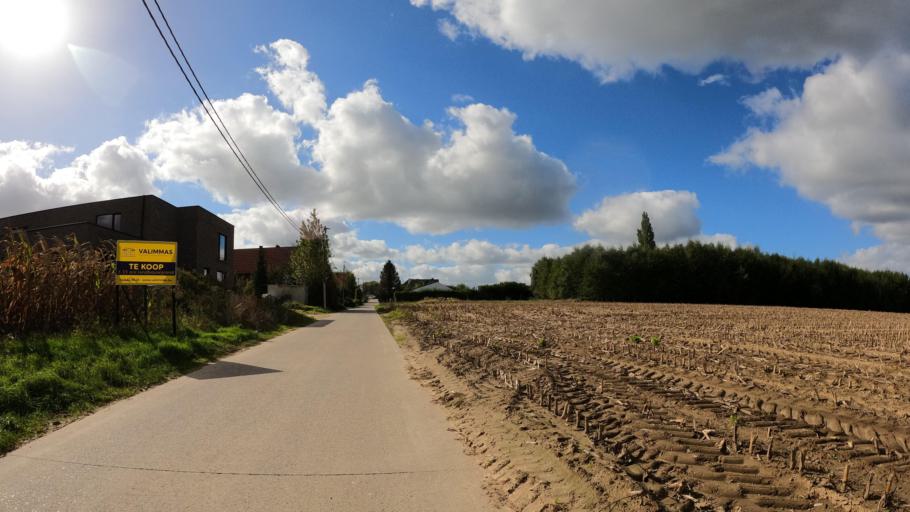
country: BE
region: Flanders
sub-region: Provincie Vlaams-Brabant
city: Asse
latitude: 50.9320
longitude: 4.1811
